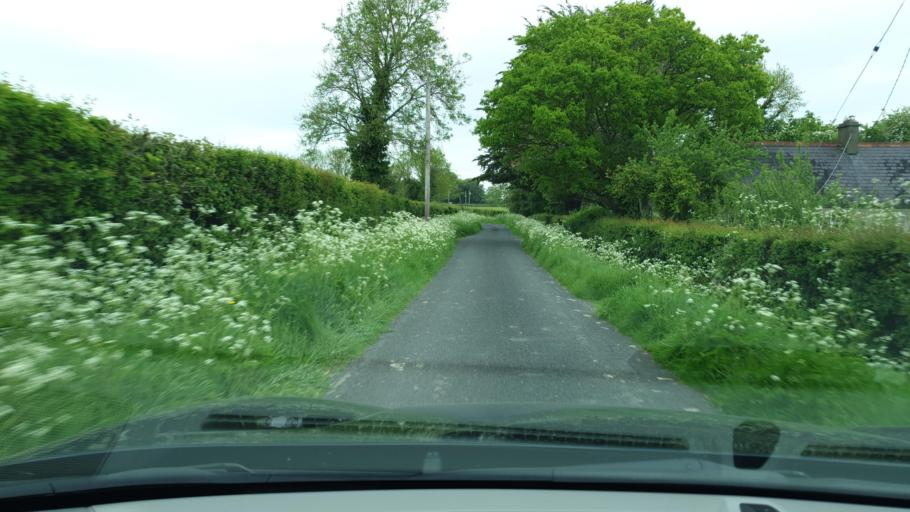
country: IE
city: Confey
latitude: 53.4338
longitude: -6.5287
